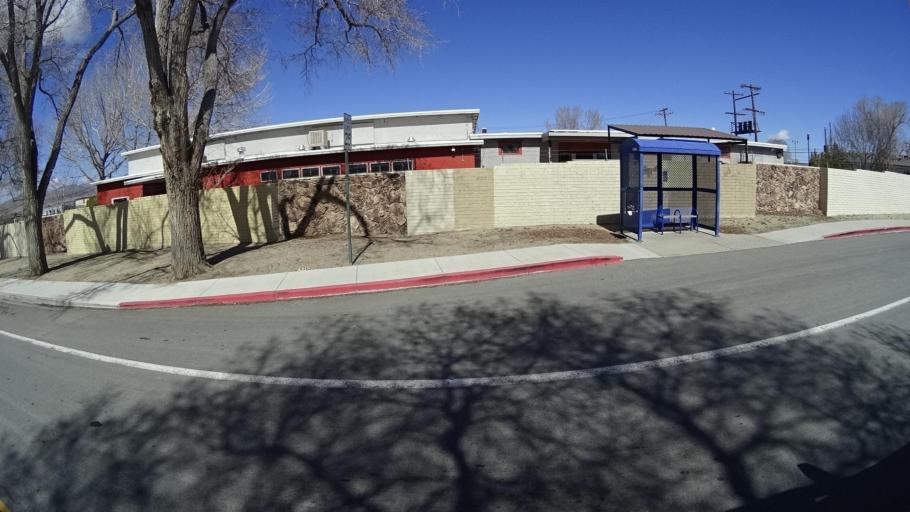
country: US
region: Nevada
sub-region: Washoe County
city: Lemmon Valley
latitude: 39.6539
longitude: -119.8768
